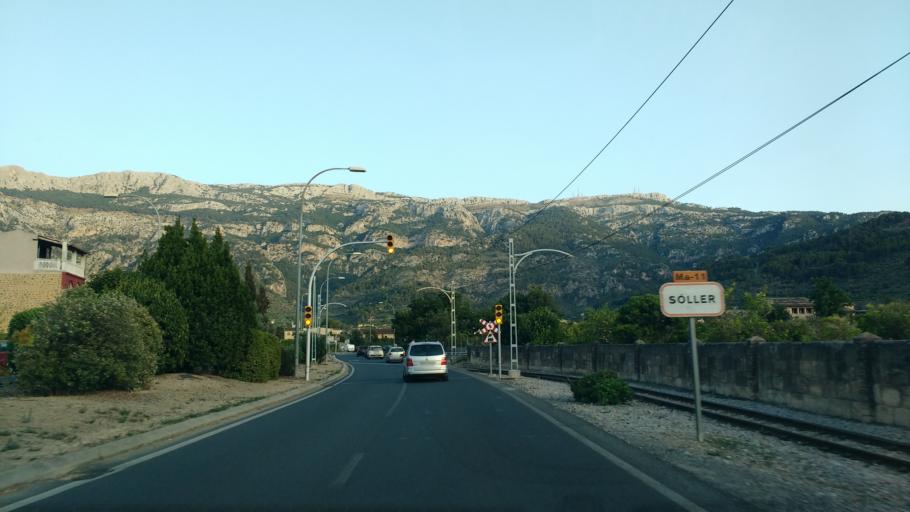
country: ES
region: Balearic Islands
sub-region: Illes Balears
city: Soller
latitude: 39.7778
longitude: 2.7048
